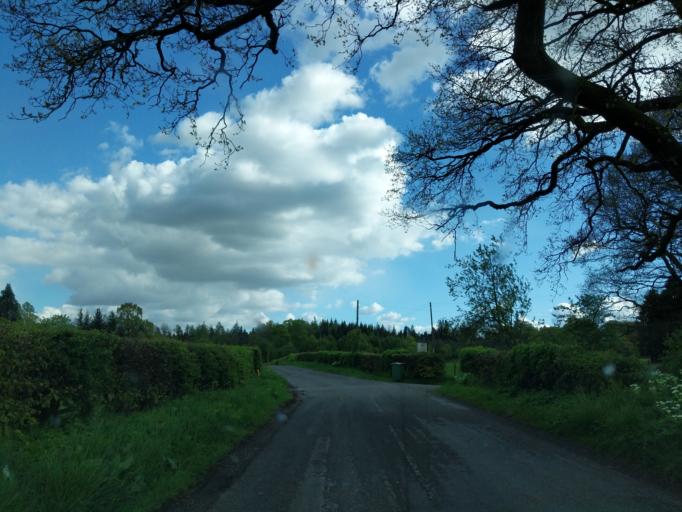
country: GB
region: Scotland
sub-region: Stirling
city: Callander
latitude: 56.1655
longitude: -4.2647
